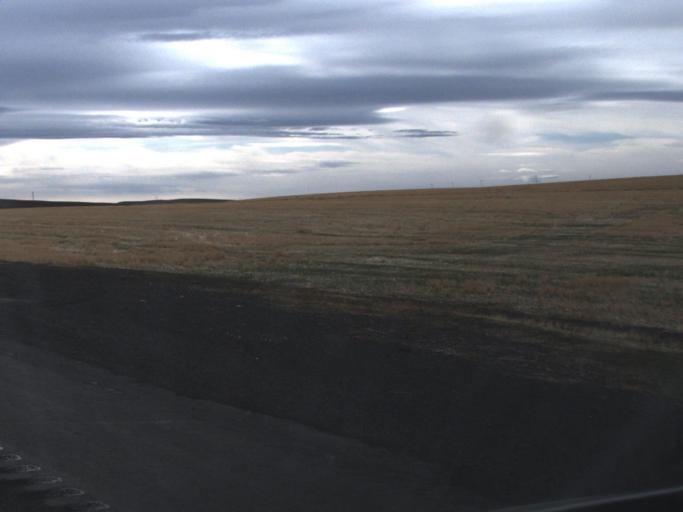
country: US
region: Washington
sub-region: Asotin County
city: Clarkston
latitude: 46.4919
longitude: -117.0738
